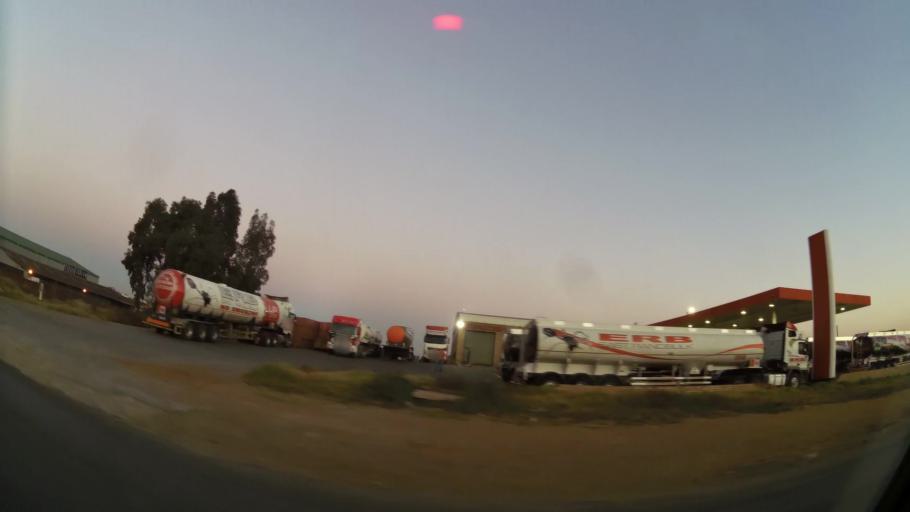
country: ZA
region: Gauteng
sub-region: Ekurhuleni Metropolitan Municipality
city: Germiston
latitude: -26.2741
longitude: 28.1731
